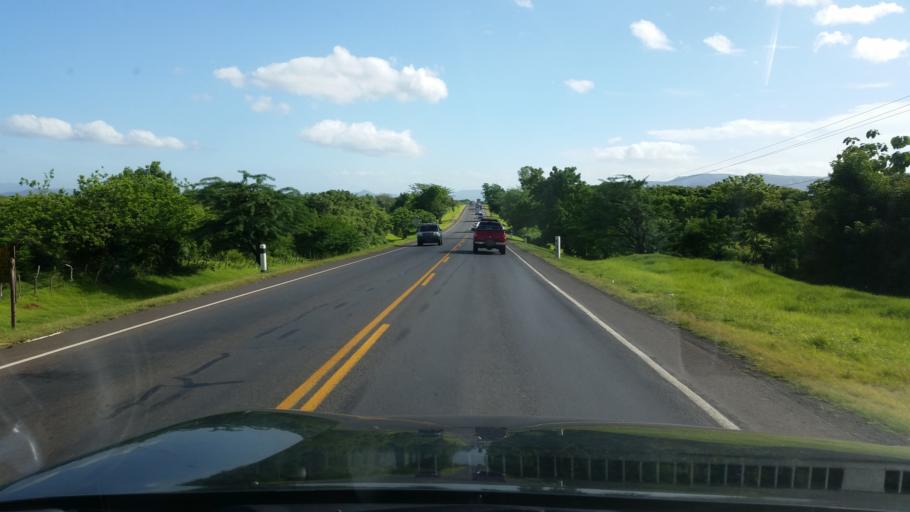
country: NI
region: Managua
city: Tipitapa
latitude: 12.3275
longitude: -86.0524
